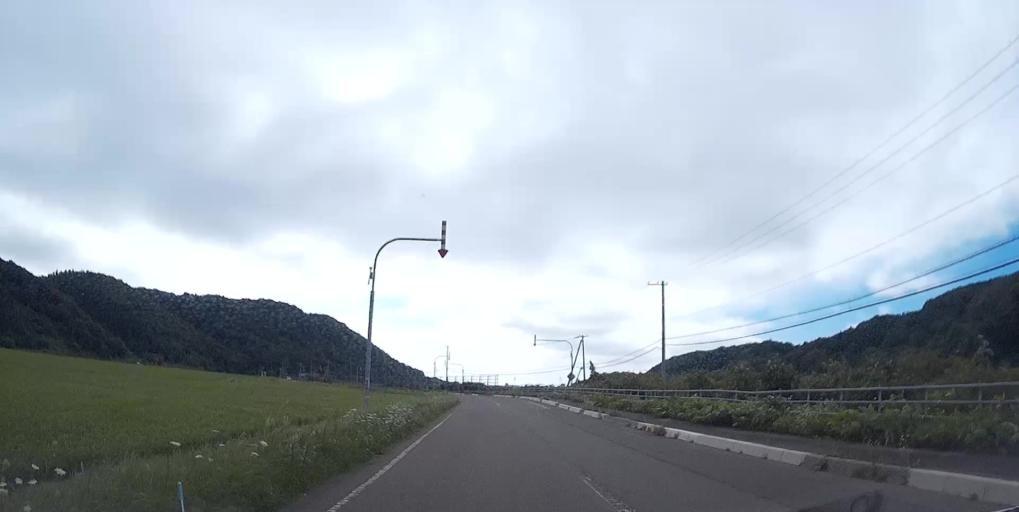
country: JP
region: Hokkaido
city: Kamiiso
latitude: 41.9738
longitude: 140.1593
